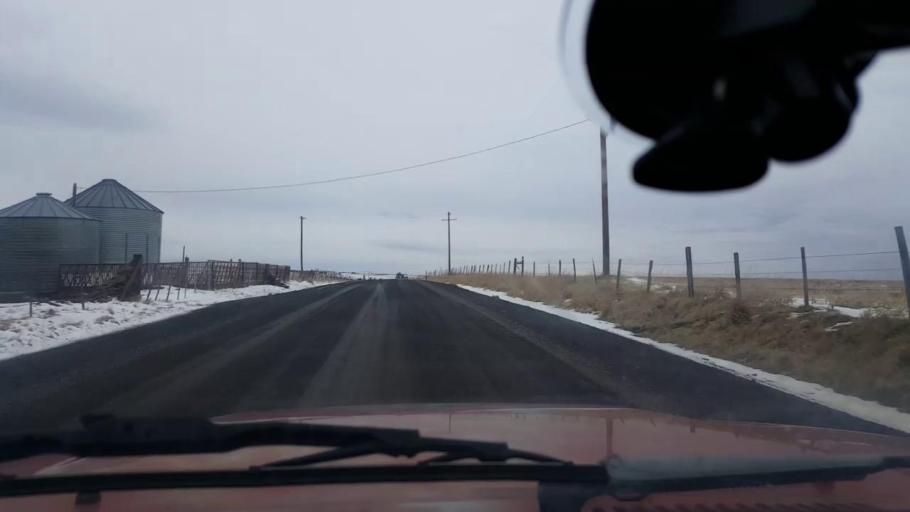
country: US
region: Washington
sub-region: Garfield County
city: Pomeroy
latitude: 46.3201
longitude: -117.4104
